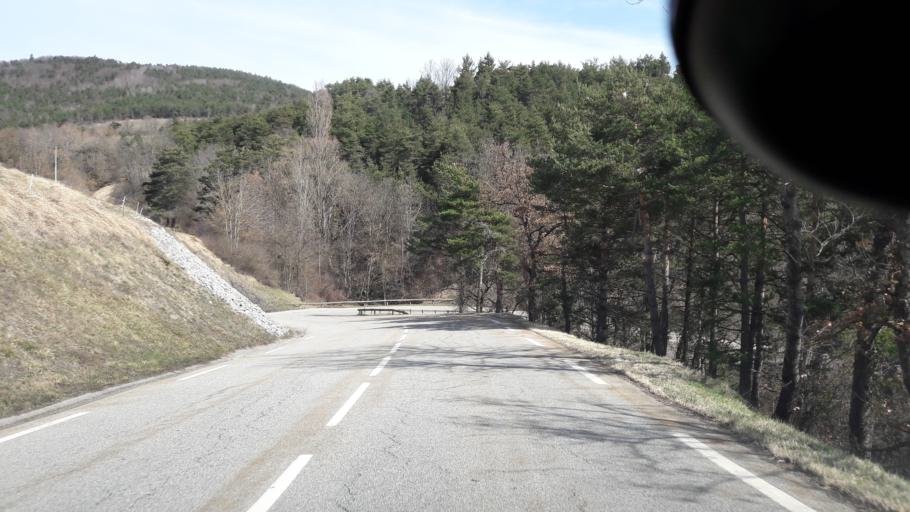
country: FR
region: Rhone-Alpes
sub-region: Departement de l'Isere
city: La Motte-Saint-Martin
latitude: 44.8733
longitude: 5.6547
